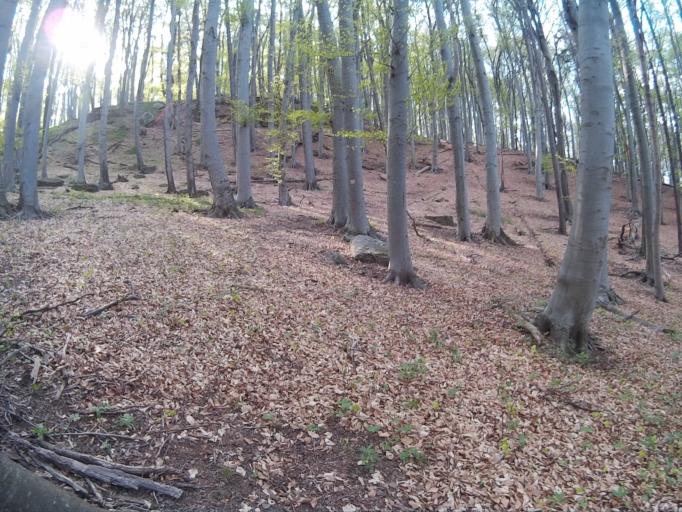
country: AT
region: Burgenland
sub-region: Politischer Bezirk Oberwart
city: Rechnitz
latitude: 47.3353
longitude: 16.4716
